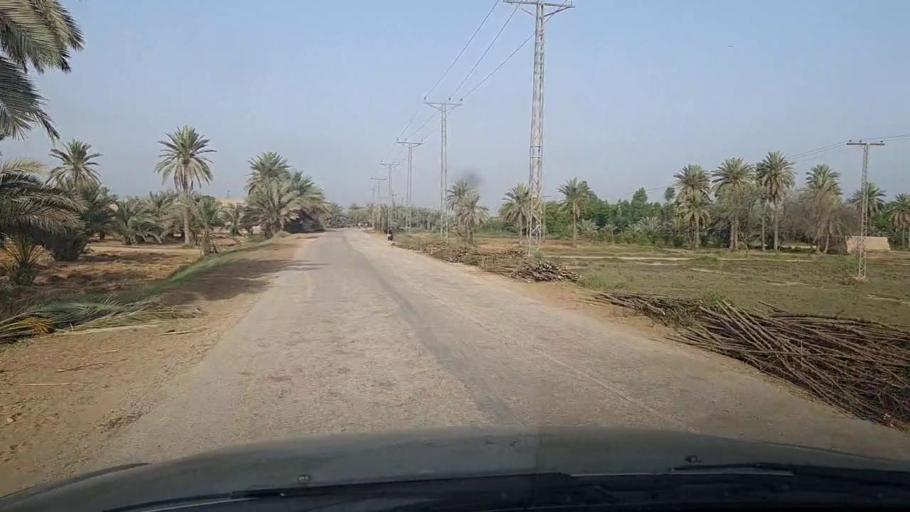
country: PK
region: Sindh
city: Pir jo Goth
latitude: 27.5715
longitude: 68.6182
